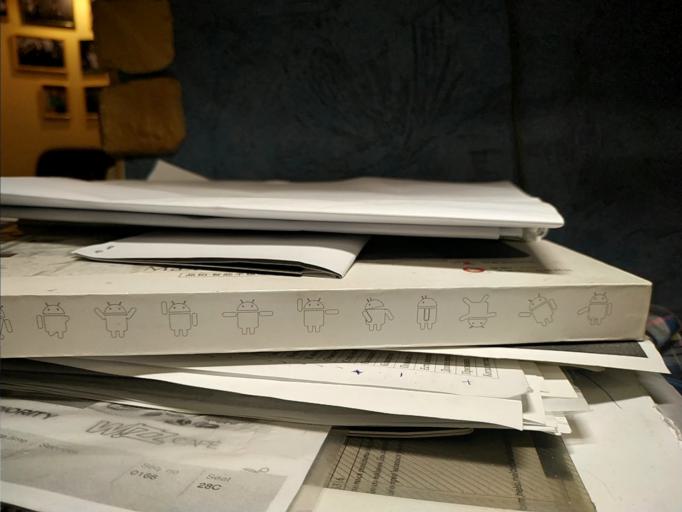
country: RU
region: Tverskaya
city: Zubtsov
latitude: 56.0855
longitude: 34.7720
